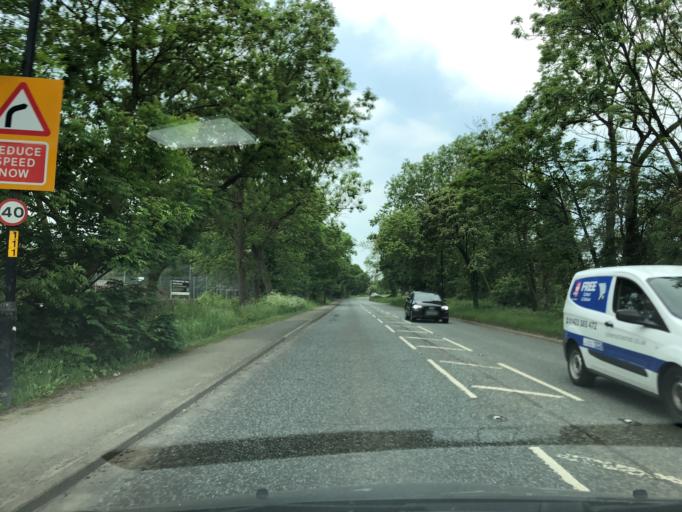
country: GB
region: England
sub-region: North Yorkshire
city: Harrogate
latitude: 54.0067
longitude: -1.5601
